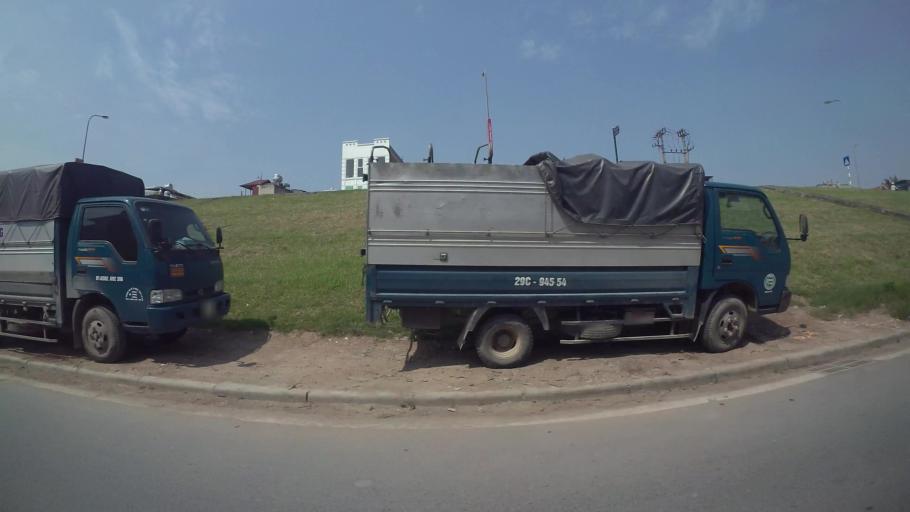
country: VN
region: Ha Noi
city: Hoan Kiem
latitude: 21.0599
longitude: 105.8640
